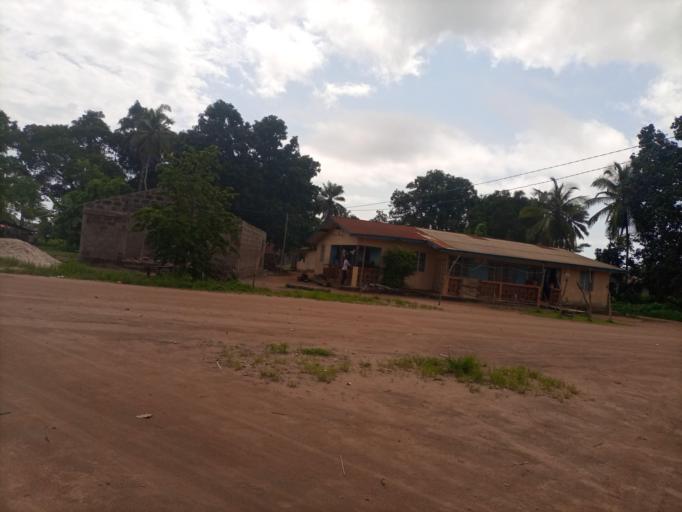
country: SL
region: Northern Province
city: Sawkta
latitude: 8.6410
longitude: -13.2128
